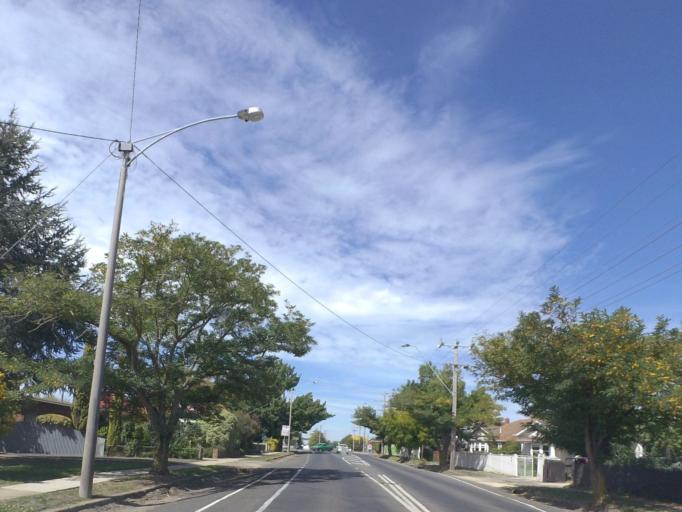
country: AU
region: Victoria
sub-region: Mount Alexander
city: Castlemaine
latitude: -37.2534
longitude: 144.4610
